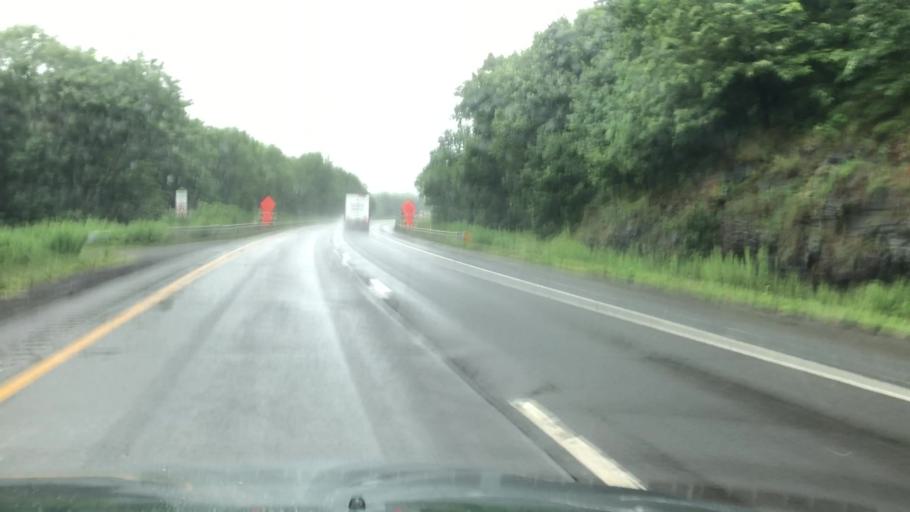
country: US
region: Pennsylvania
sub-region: Pike County
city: Conashaugh Lakes
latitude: 41.3464
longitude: -74.9935
